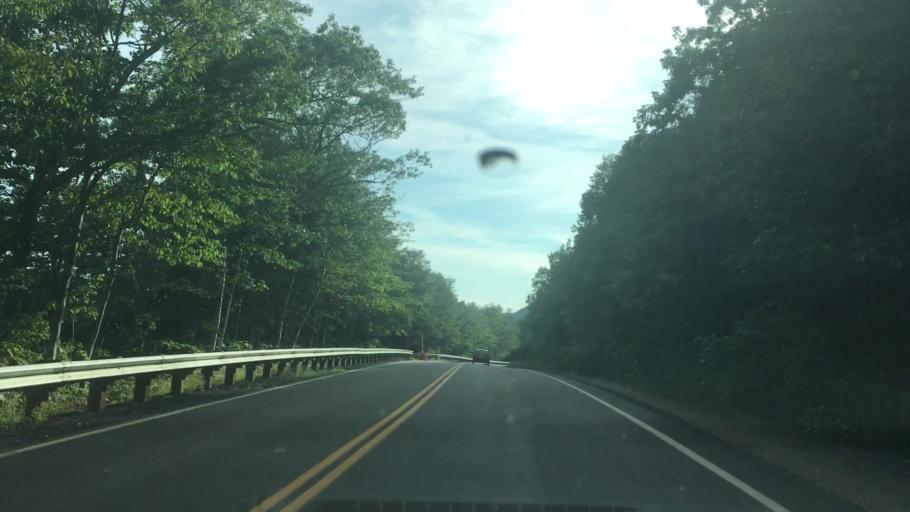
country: CA
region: Nova Scotia
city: Sydney Mines
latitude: 46.8254
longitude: -60.6240
